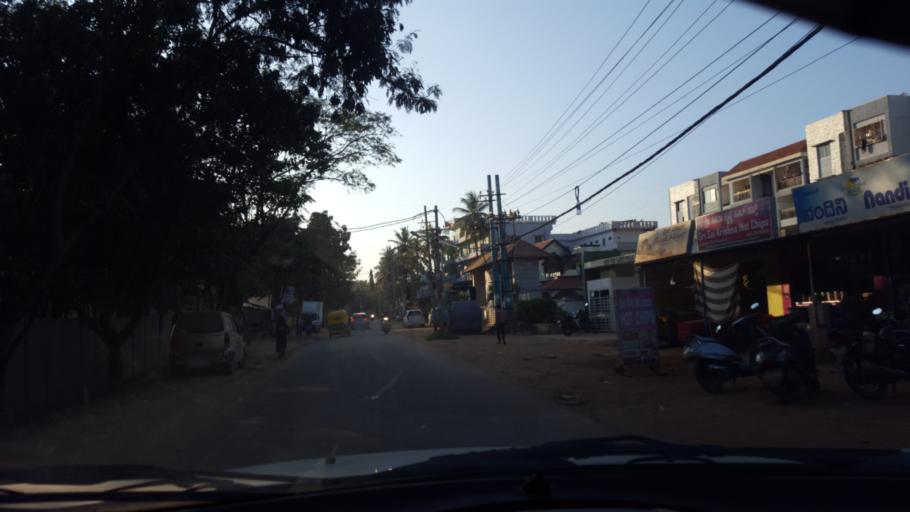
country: IN
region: Karnataka
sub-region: Bangalore Urban
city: Bangalore
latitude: 12.9393
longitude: 77.7307
